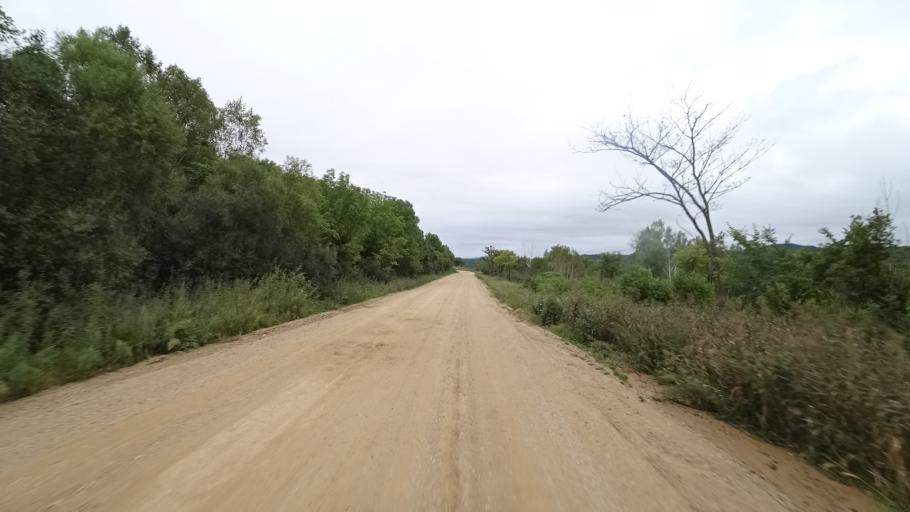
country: RU
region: Primorskiy
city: Rettikhovka
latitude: 44.1780
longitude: 132.8276
